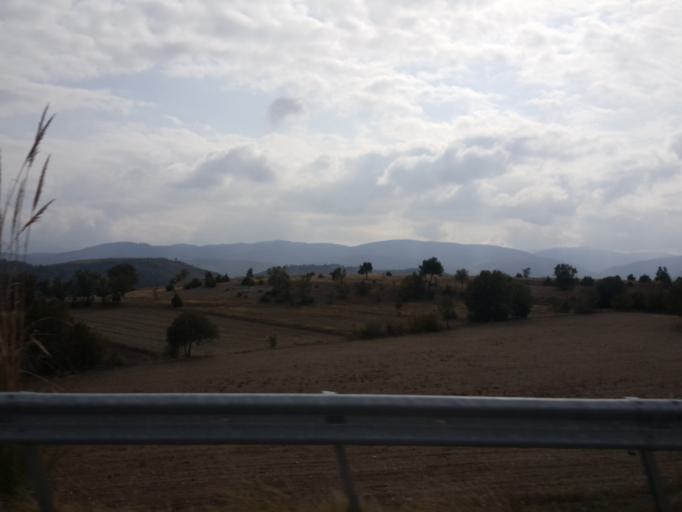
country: TR
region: Sinop
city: Sarayduzu
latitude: 41.3442
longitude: 34.8184
